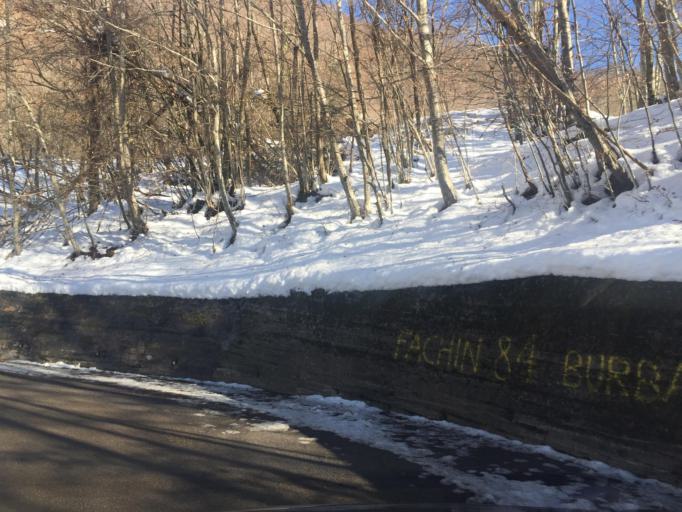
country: IT
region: Friuli Venezia Giulia
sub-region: Provincia di Udine
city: Lauco
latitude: 46.4434
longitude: 12.9536
